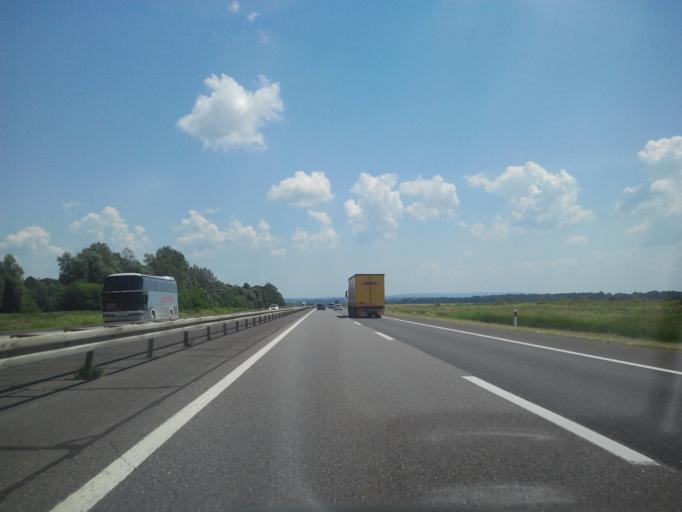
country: HR
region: Zagrebacka
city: Kriz
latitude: 45.6842
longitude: 16.4246
